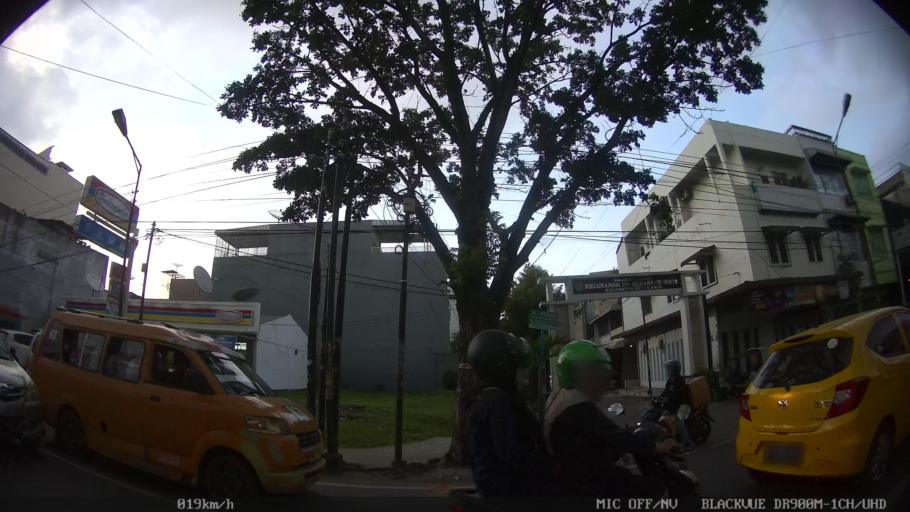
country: ID
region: North Sumatra
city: Medan
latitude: 3.5821
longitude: 98.6979
